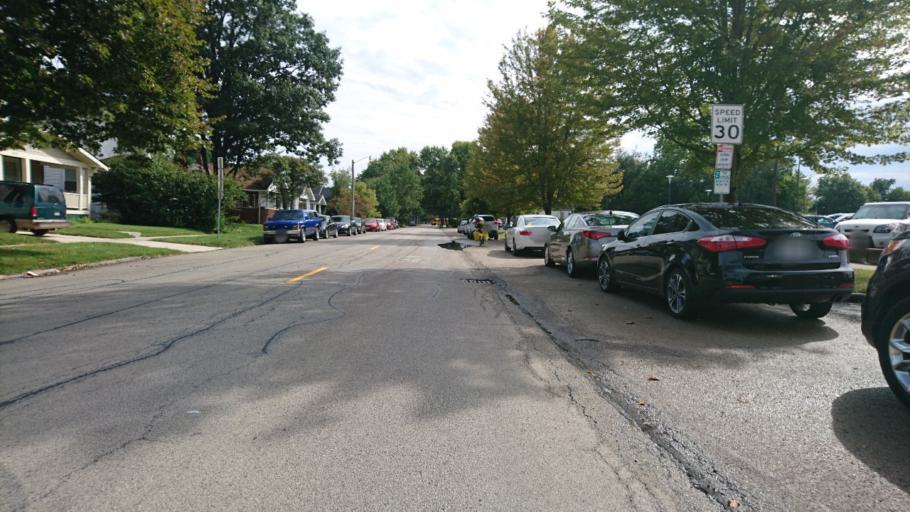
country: US
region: Illinois
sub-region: Sangamon County
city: Springfield
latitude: 39.7862
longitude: -89.6537
